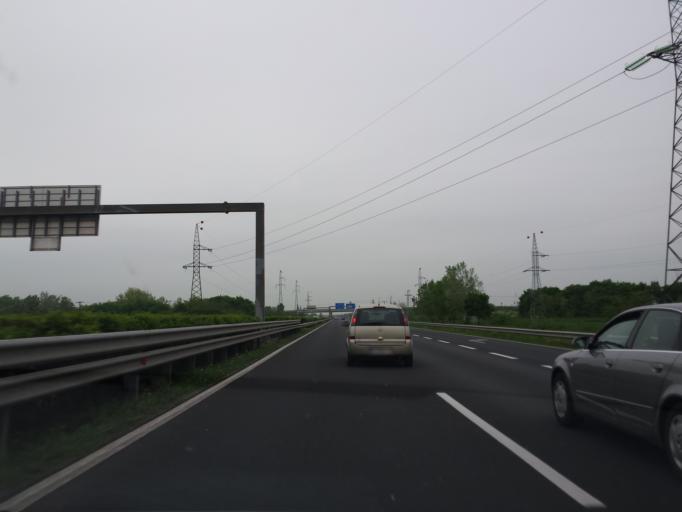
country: HU
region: Gyor-Moson-Sopron
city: Mosonmagyarovar
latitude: 47.8488
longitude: 17.2526
